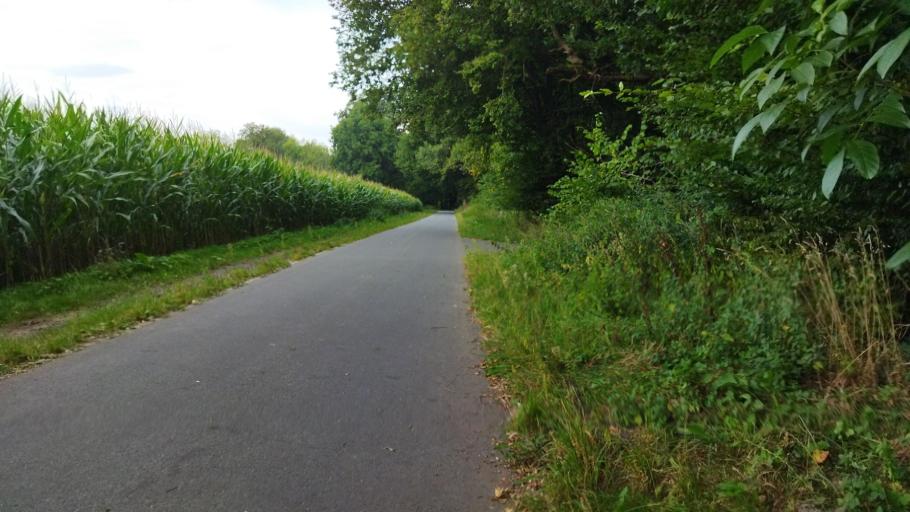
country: DE
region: North Rhine-Westphalia
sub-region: Regierungsbezirk Munster
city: Telgte
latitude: 52.0139
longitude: 7.7638
